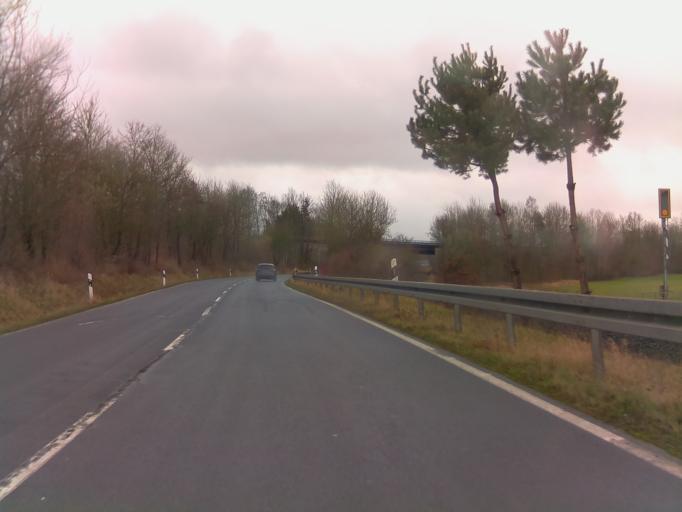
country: DE
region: Hesse
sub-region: Regierungsbezirk Kassel
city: Eichenzell
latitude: 50.5046
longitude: 9.6823
